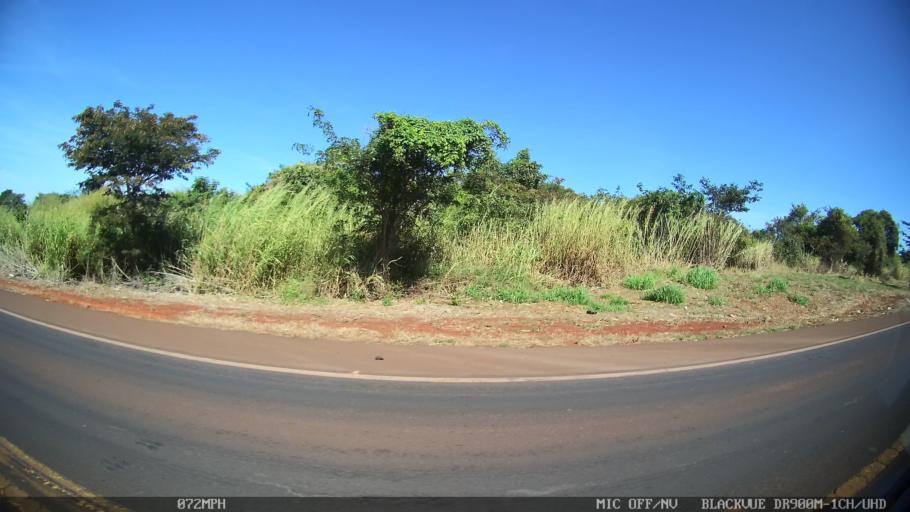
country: BR
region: Sao Paulo
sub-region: Ipua
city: Ipua
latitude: -20.4936
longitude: -48.0321
